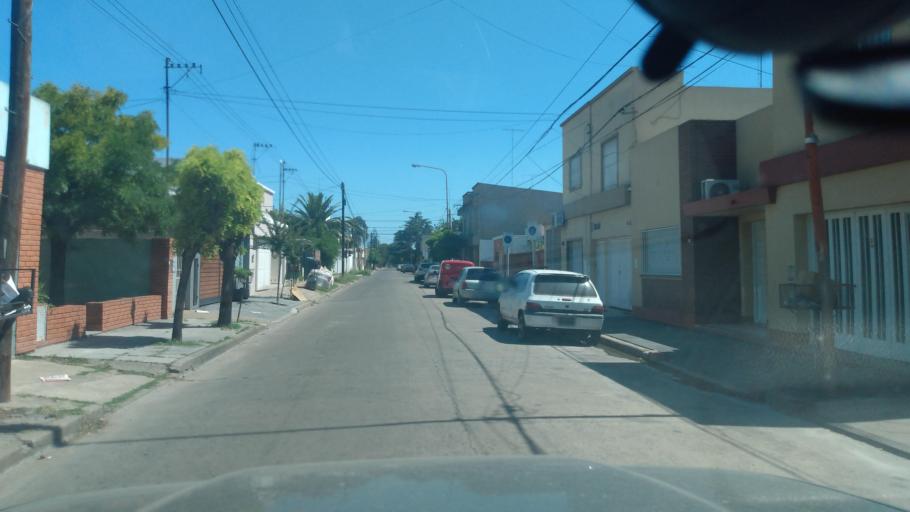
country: AR
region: Buenos Aires
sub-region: Partido de Lujan
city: Lujan
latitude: -34.5634
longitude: -59.1040
